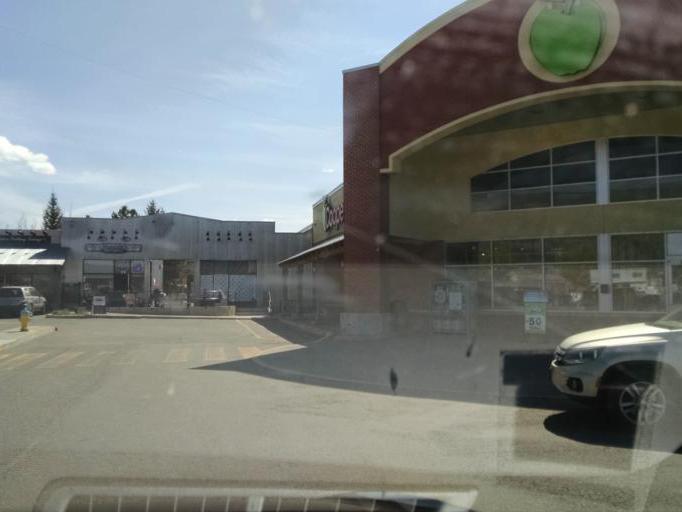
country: CA
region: British Columbia
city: Merritt
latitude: 50.1076
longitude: -120.7876
